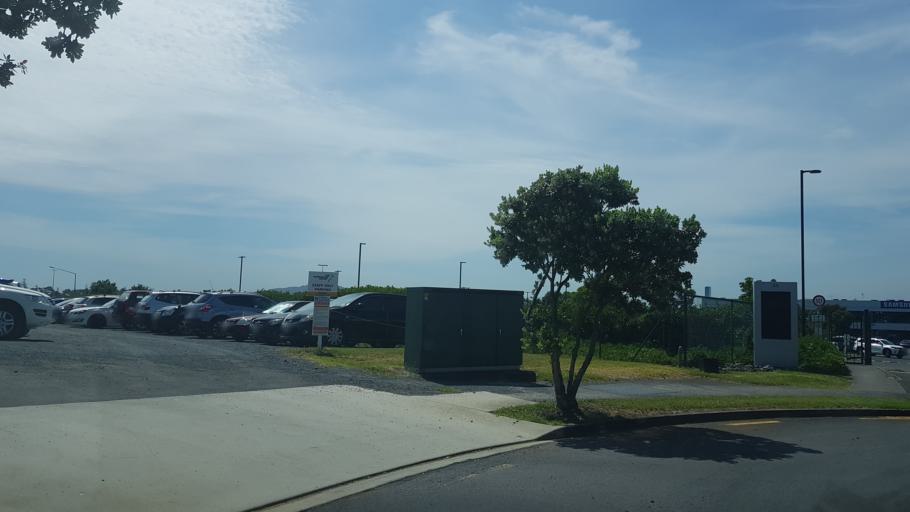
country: NZ
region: Auckland
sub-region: Auckland
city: North Shore
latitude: -36.8008
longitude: 174.7581
